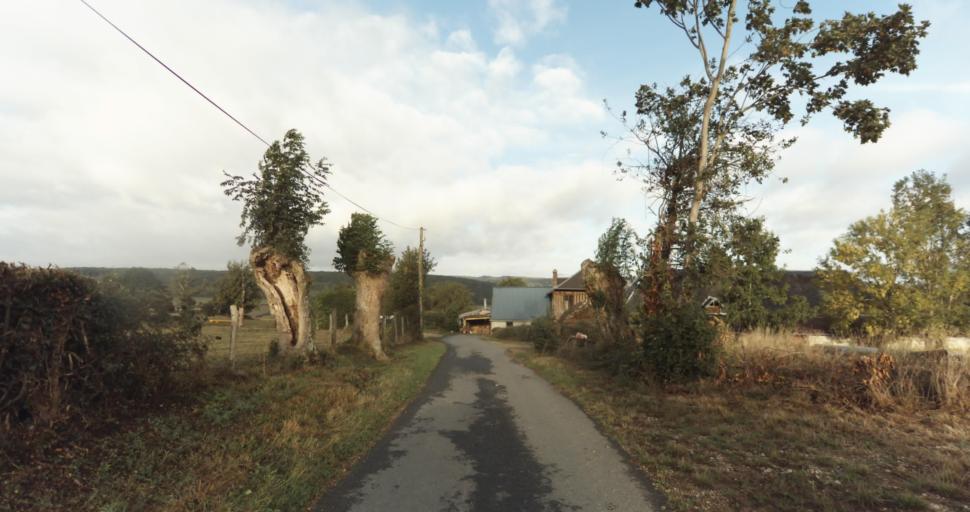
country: FR
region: Lower Normandy
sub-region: Departement de l'Orne
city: Vimoutiers
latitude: 48.9065
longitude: 0.2244
